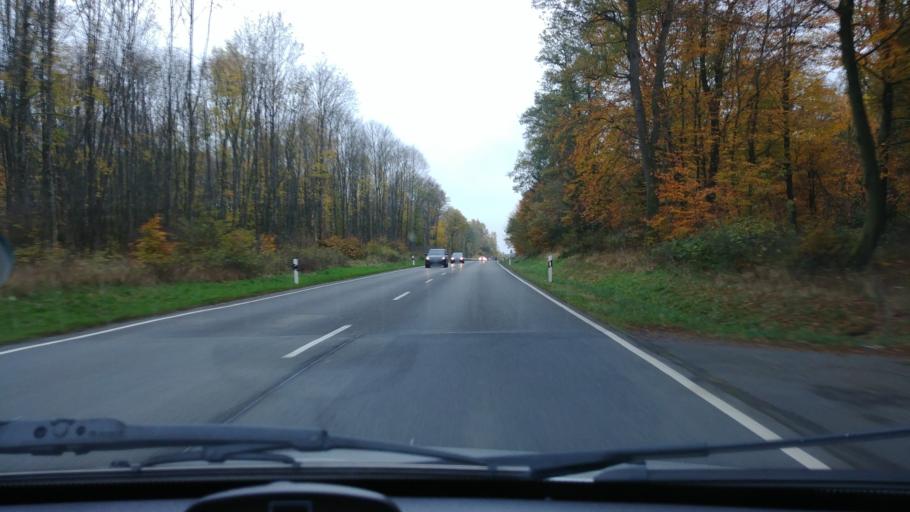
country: DE
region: Rheinland-Pfalz
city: Langenhahn
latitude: 50.5788
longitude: 7.9343
